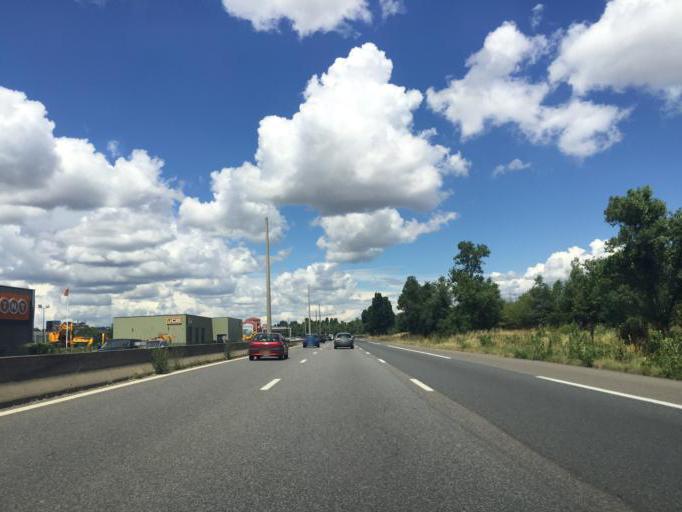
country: FR
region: Rhone-Alpes
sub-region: Departement du Rhone
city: Pierre-Benite
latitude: 45.7000
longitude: 4.8358
